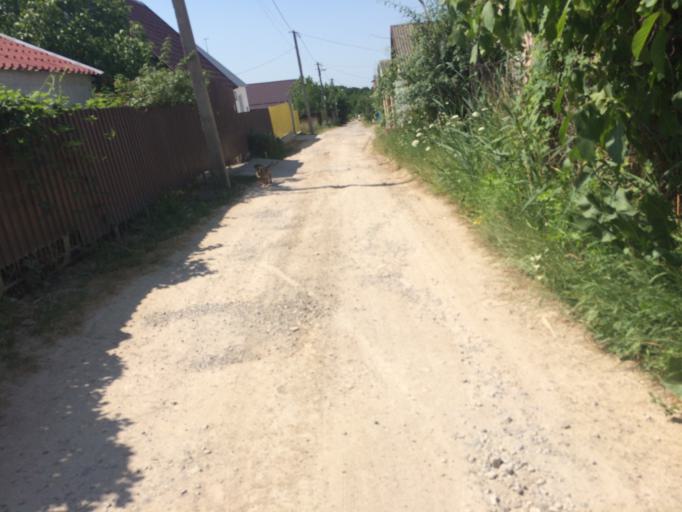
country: RU
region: Stavropol'skiy
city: Tatarka
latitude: 44.9824
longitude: 41.9412
